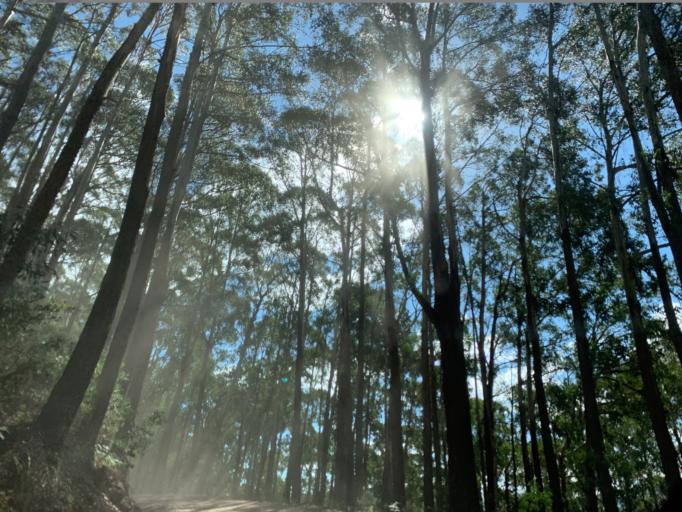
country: AU
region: Victoria
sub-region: Mansfield
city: Mansfield
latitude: -37.0967
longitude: 146.4665
